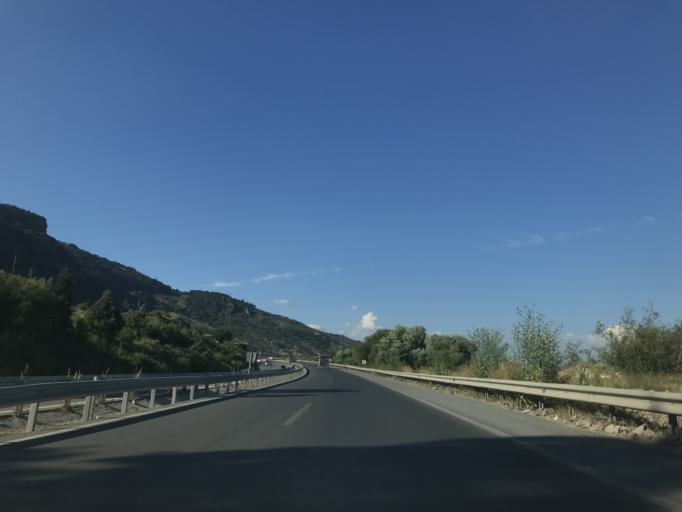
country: TR
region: Aydin
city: Ortaklar
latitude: 37.8148
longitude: 27.4857
